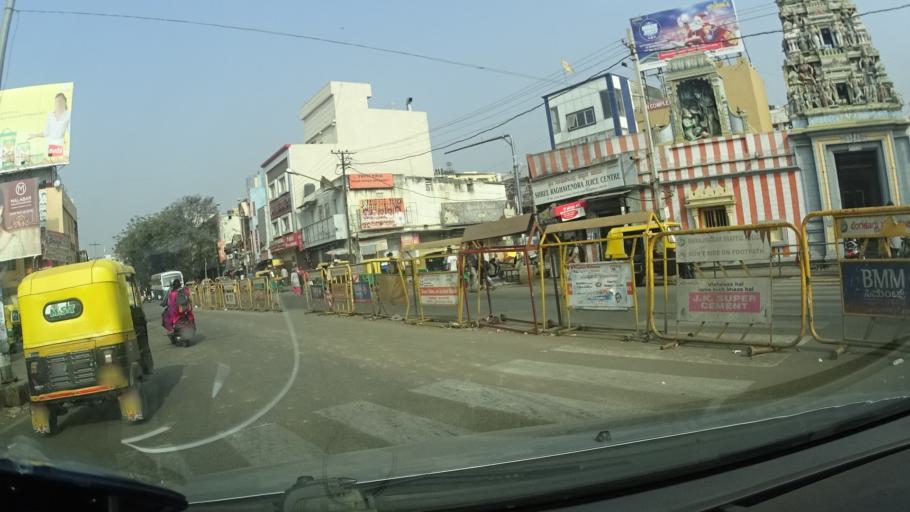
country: IN
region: Karnataka
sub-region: Bangalore Urban
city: Bangalore
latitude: 12.9840
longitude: 77.6035
